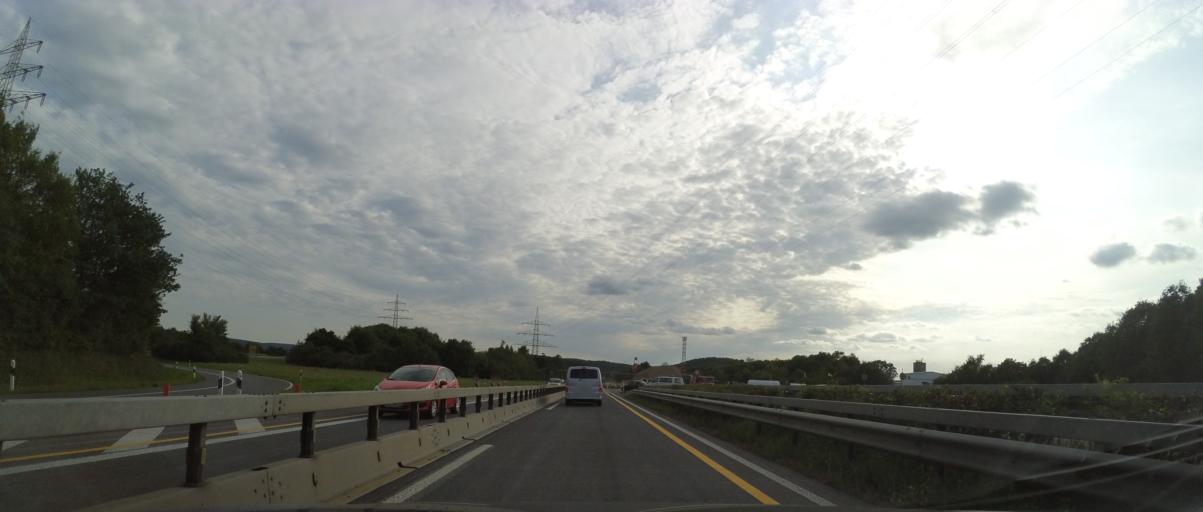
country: DE
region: Rheinland-Pfalz
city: Wittlich
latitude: 49.9818
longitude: 6.9151
